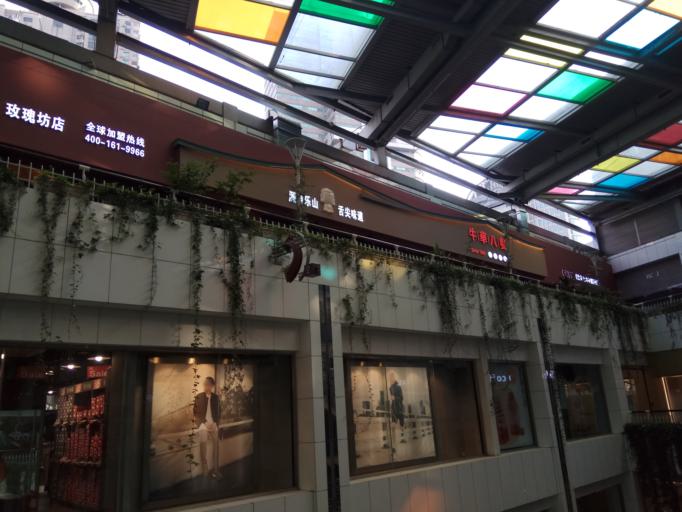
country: CN
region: Shanghai Shi
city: Changning
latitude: 31.2209
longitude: 121.4143
